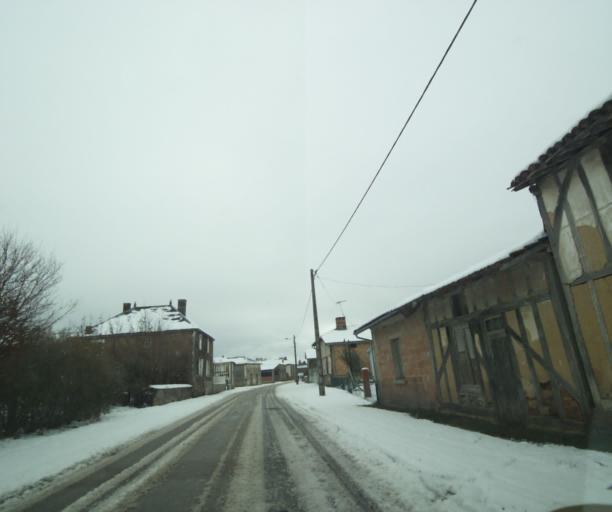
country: FR
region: Champagne-Ardenne
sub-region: Departement de la Haute-Marne
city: Montier-en-Der
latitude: 48.4330
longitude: 4.7271
